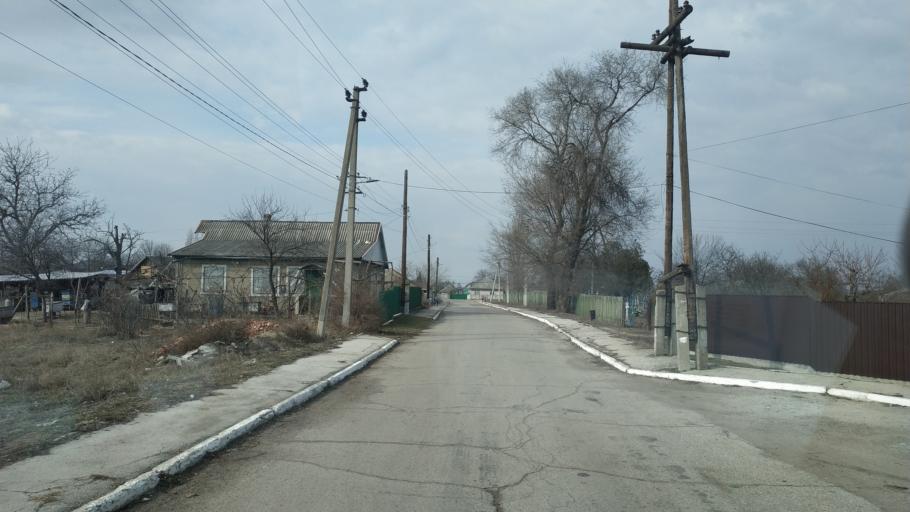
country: MD
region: Anenii Noi
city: Anenii Noi
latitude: 46.9018
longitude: 29.1368
